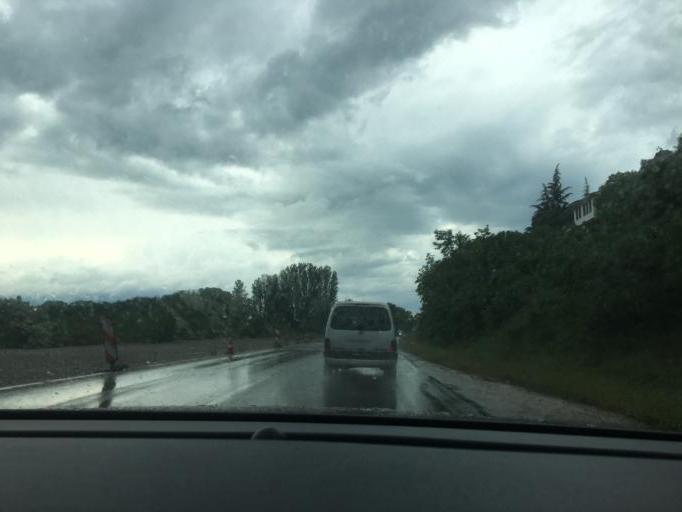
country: MK
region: Ohrid
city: Ohrid
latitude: 41.1412
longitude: 20.7618
